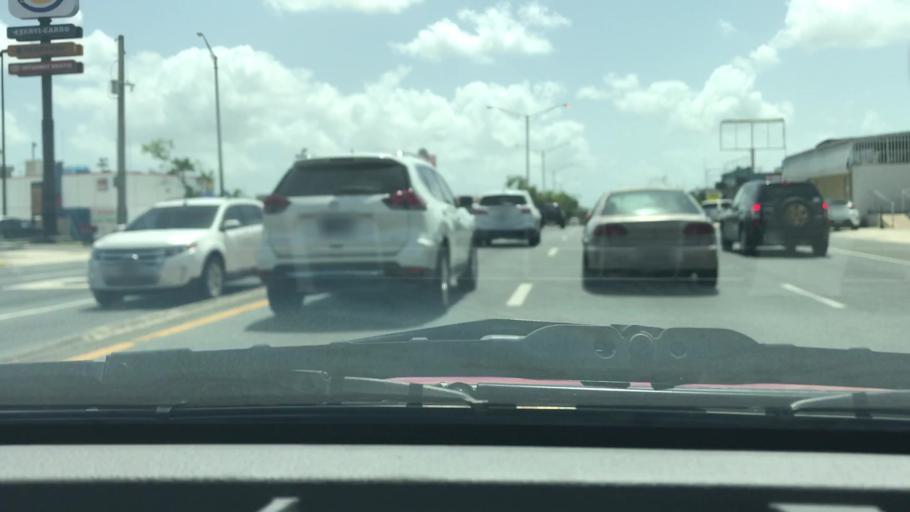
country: PR
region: Bayamon
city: Bayamon
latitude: 18.3651
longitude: -66.1754
